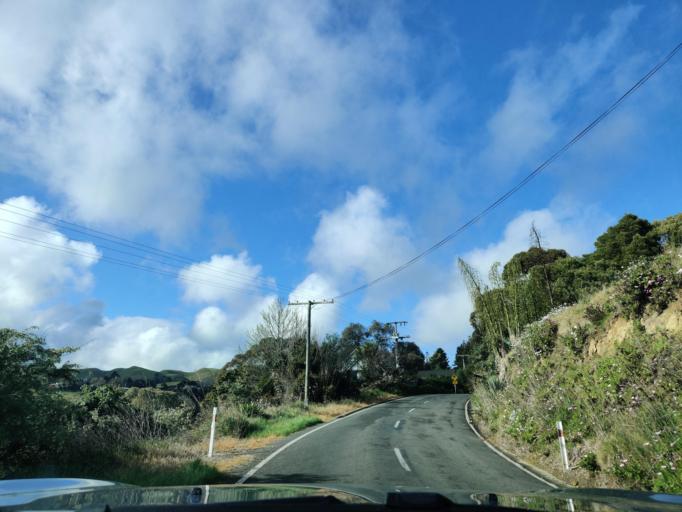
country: NZ
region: Hawke's Bay
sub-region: Hastings District
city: Hastings
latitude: -39.6799
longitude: 176.8967
